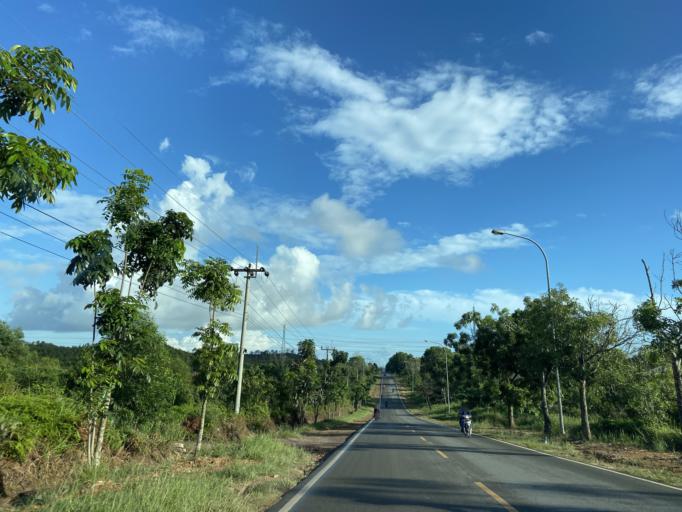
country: SG
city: Singapore
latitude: 1.0150
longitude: 104.0184
